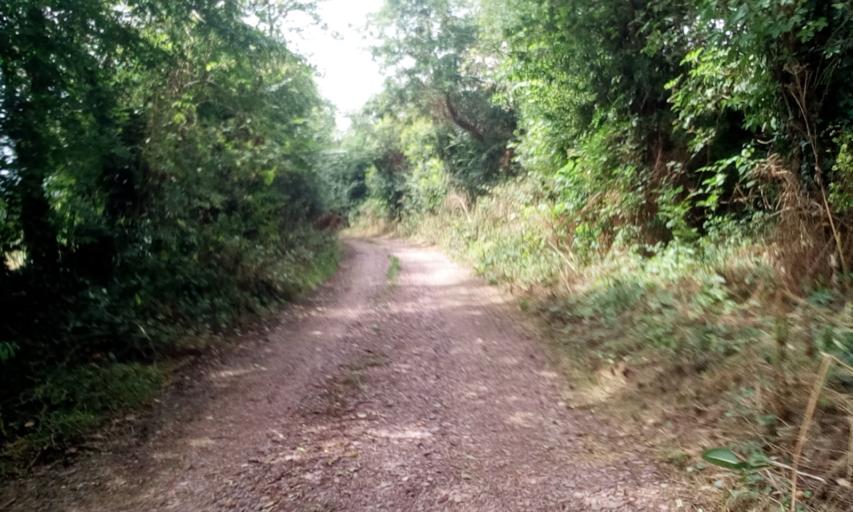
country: FR
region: Lower Normandy
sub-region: Departement du Calvados
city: Cheux
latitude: 49.1854
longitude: -0.5353
